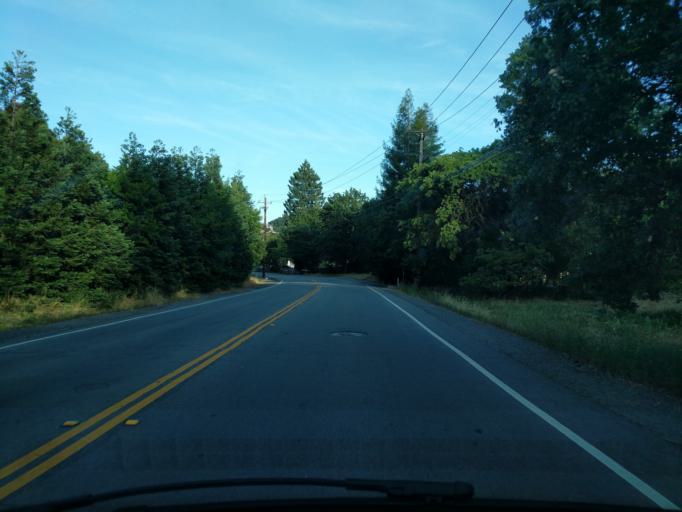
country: US
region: California
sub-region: Contra Costa County
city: Saranap
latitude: 37.8752
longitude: -122.0661
